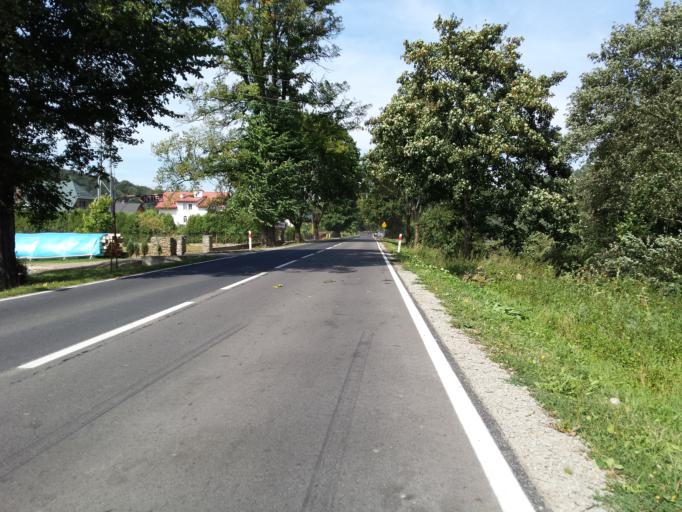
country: PL
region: Subcarpathian Voivodeship
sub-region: Powiat leski
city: Lesko
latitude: 49.4570
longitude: 22.3395
